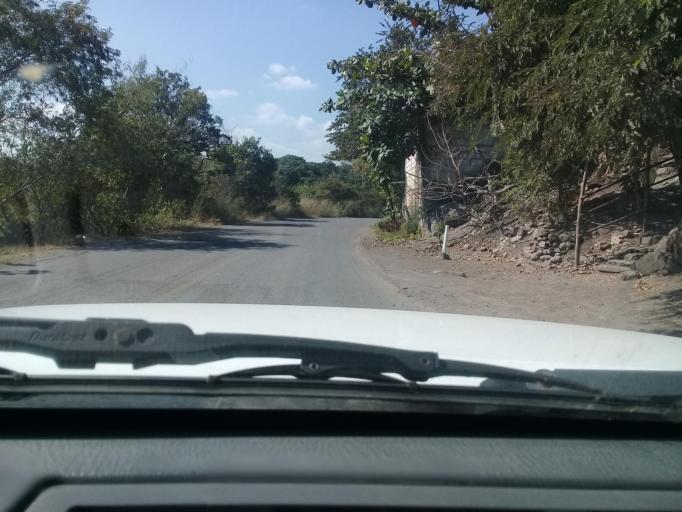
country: MX
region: Veracruz
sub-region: Emiliano Zapata
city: Plan del Rio
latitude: 19.4253
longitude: -96.6092
